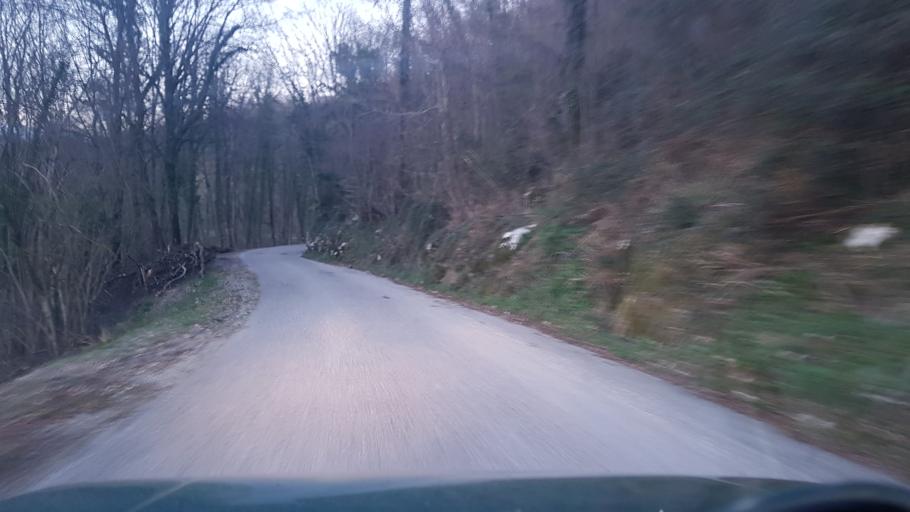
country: SI
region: Kanal
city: Kanal
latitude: 46.0781
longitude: 13.6468
